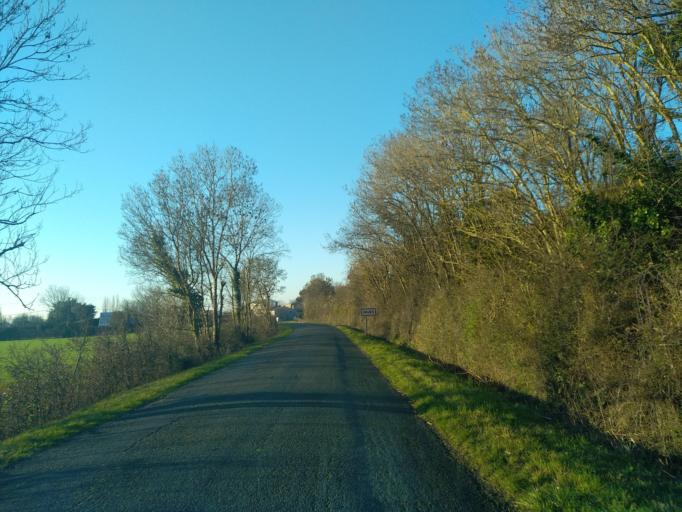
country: FR
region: Pays de la Loire
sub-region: Departement de la Vendee
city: Triaize
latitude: 46.3960
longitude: -1.2985
